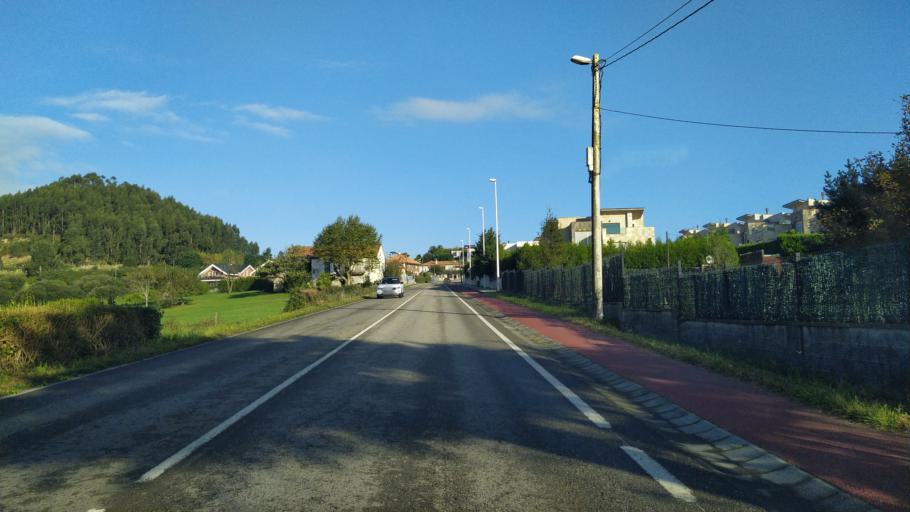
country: ES
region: Cantabria
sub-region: Provincia de Cantabria
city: Santa Cruz de Bezana
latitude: 43.4365
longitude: -3.9194
